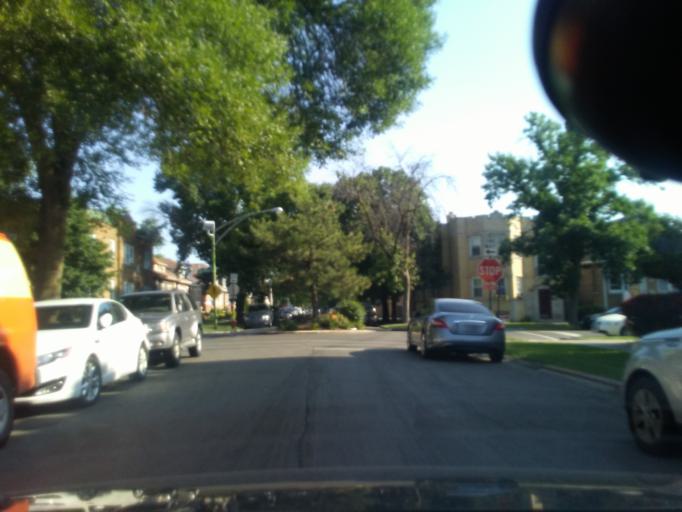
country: US
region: Illinois
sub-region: Cook County
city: Elmwood Park
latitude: 41.9348
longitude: -87.7614
